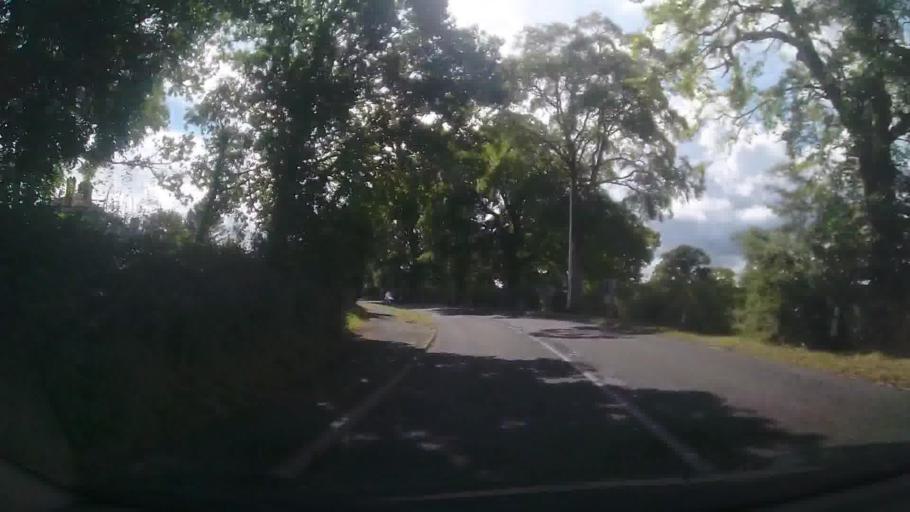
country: GB
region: Wales
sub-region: Sir Powys
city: Llandrindod Wells
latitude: 52.2134
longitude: -3.3933
